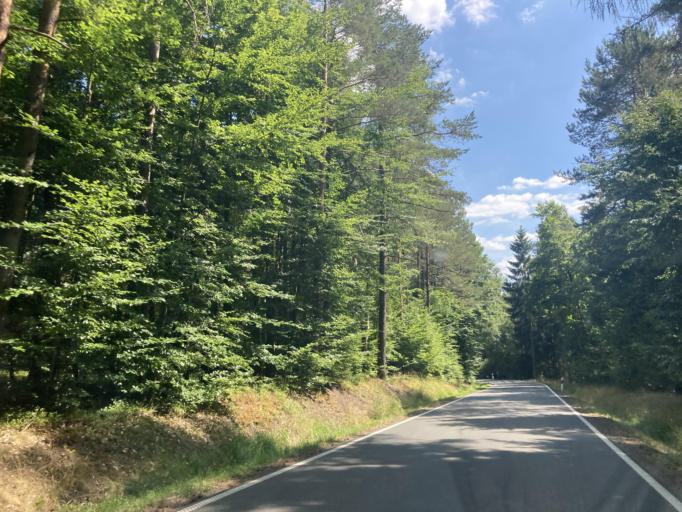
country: DE
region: Hesse
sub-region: Regierungsbezirk Kassel
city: Ottrau
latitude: 50.7299
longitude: 9.3917
